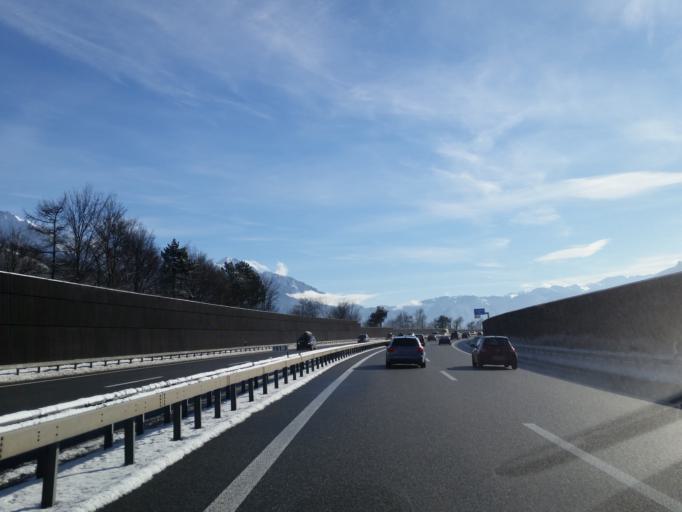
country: CH
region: Saint Gallen
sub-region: Wahlkreis Sarganserland
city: Sargans
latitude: 47.0530
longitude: 9.4250
